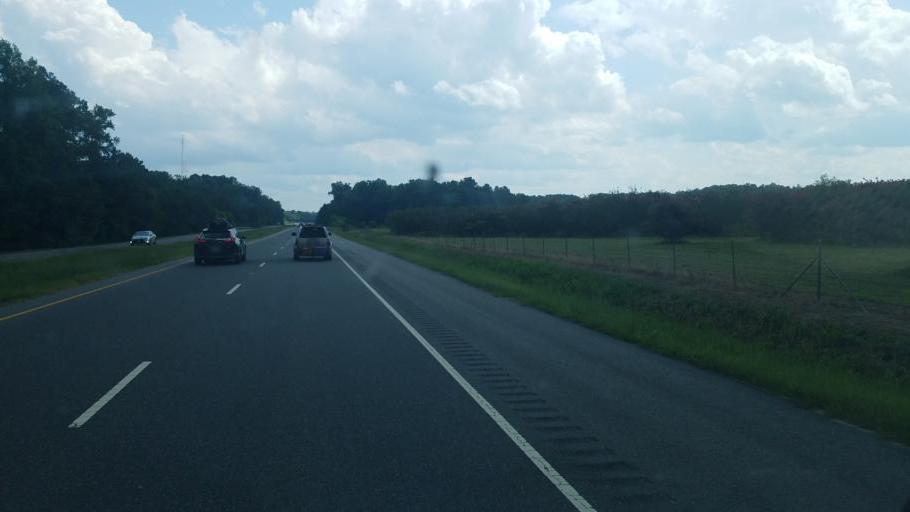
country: US
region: North Carolina
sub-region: Currituck County
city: Moyock
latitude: 36.6418
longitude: -76.2195
